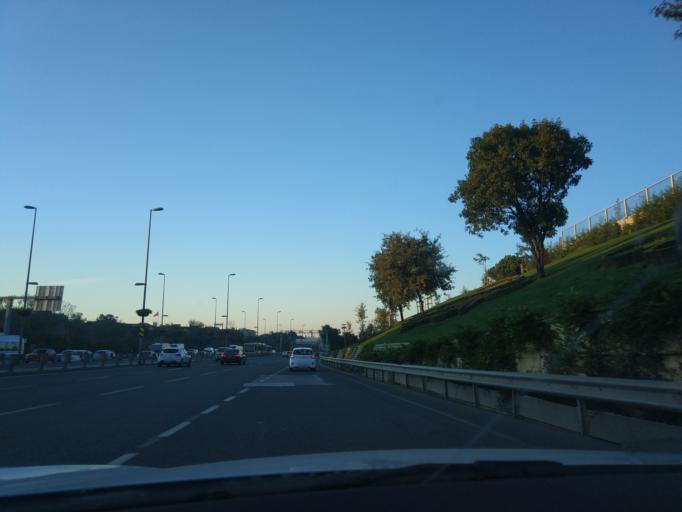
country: TR
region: Istanbul
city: UEskuedar
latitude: 41.0263
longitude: 29.0464
